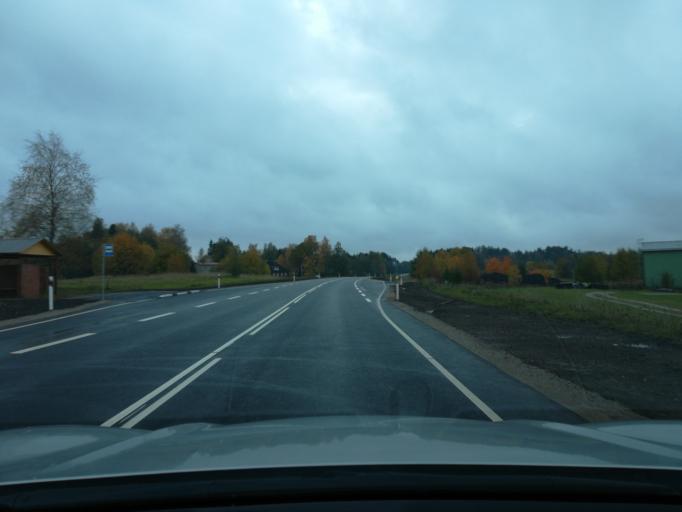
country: EE
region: Ida-Virumaa
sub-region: Johvi vald
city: Johvi
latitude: 59.1450
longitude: 27.3566
